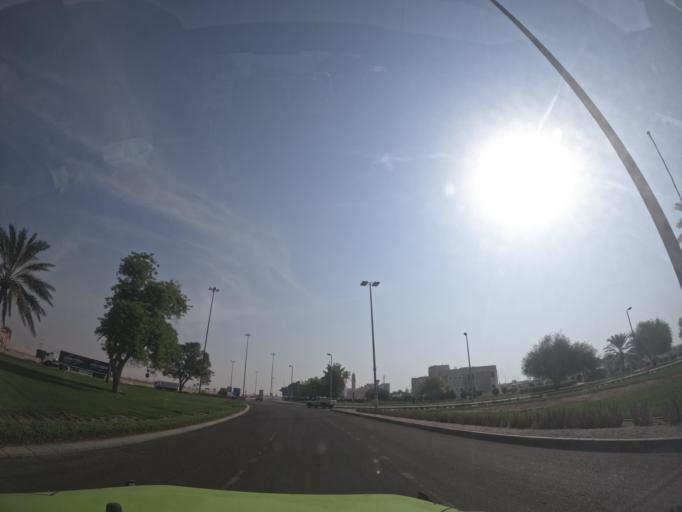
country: AE
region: Abu Dhabi
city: Al Ain
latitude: 24.4667
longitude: 55.3266
